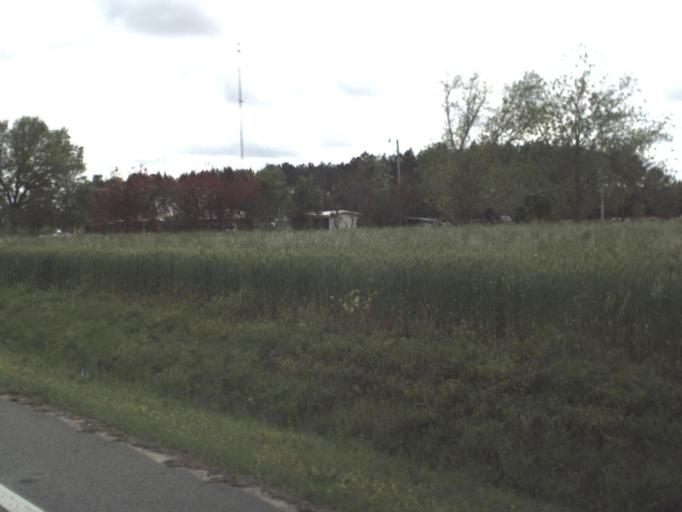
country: US
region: Alabama
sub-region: Escambia County
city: East Brewton
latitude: 30.9276
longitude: -87.0222
